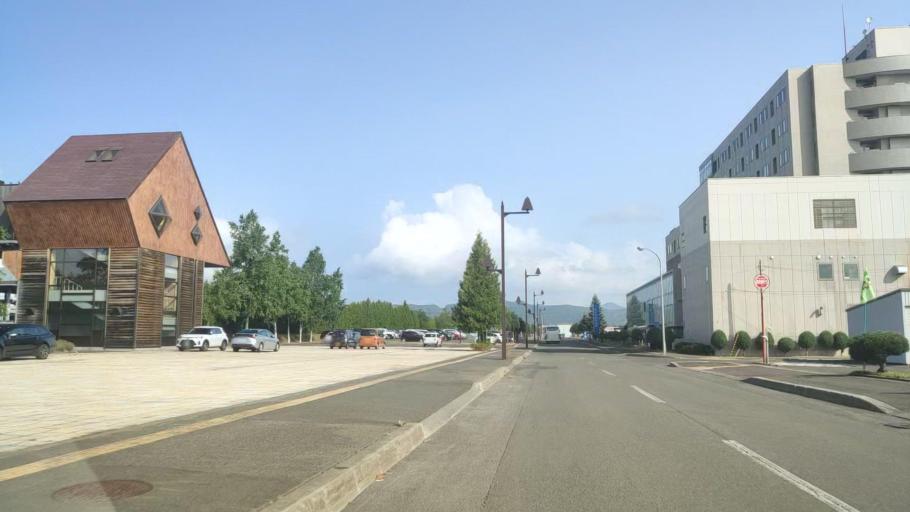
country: JP
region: Hokkaido
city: Shimo-furano
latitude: 43.3465
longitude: 142.3927
